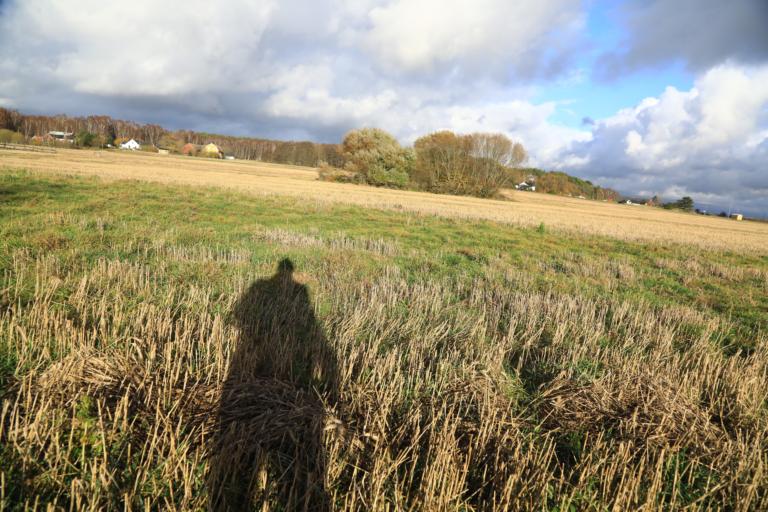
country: SE
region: Halland
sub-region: Varbergs Kommun
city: Traslovslage
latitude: 57.0885
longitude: 12.2831
